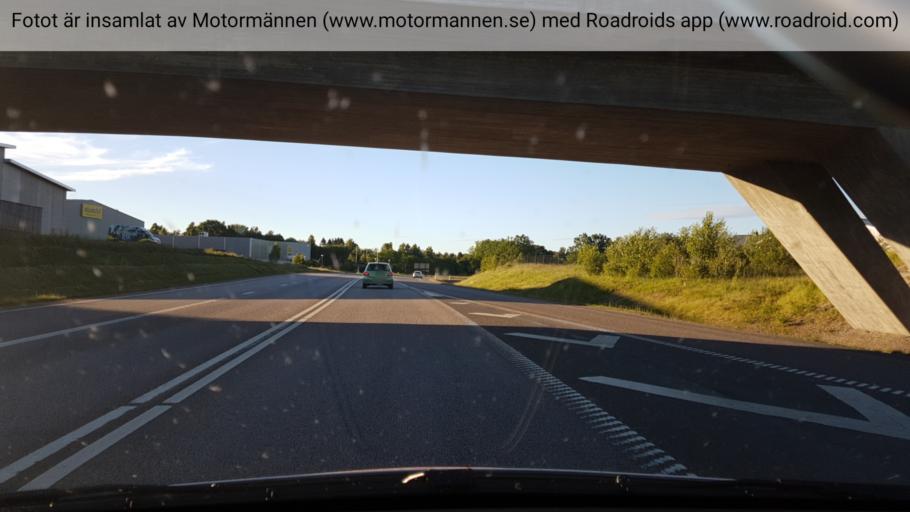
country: SE
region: Vaestra Goetaland
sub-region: Skovde Kommun
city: Skoevde
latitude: 58.4127
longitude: 13.8811
